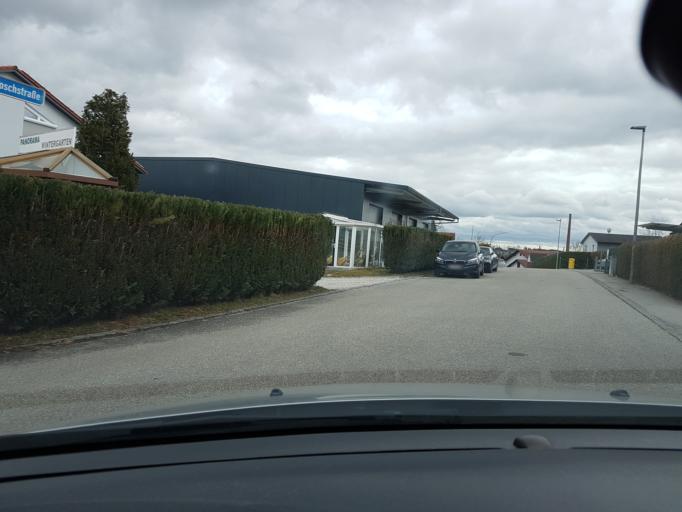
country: DE
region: Bavaria
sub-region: Lower Bavaria
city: Geisenhausen
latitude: 48.4801
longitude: 12.2463
